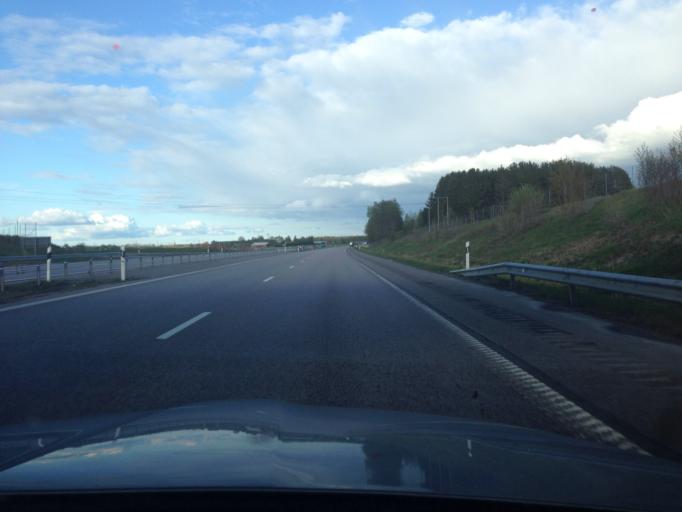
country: SE
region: OEstergoetland
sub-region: Mjolby Kommun
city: Mantorp
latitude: 58.3563
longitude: 15.2236
